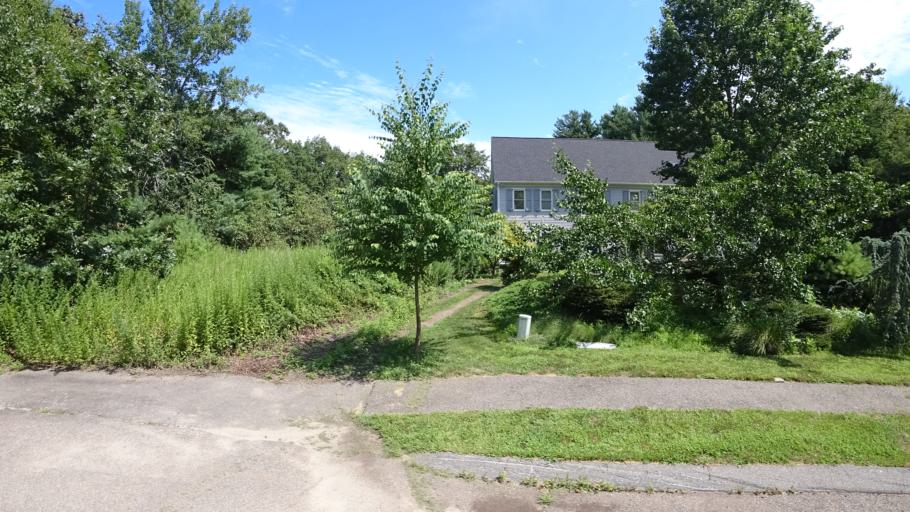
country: US
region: Massachusetts
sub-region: Norfolk County
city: Dedham
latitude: 42.2384
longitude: -71.1899
